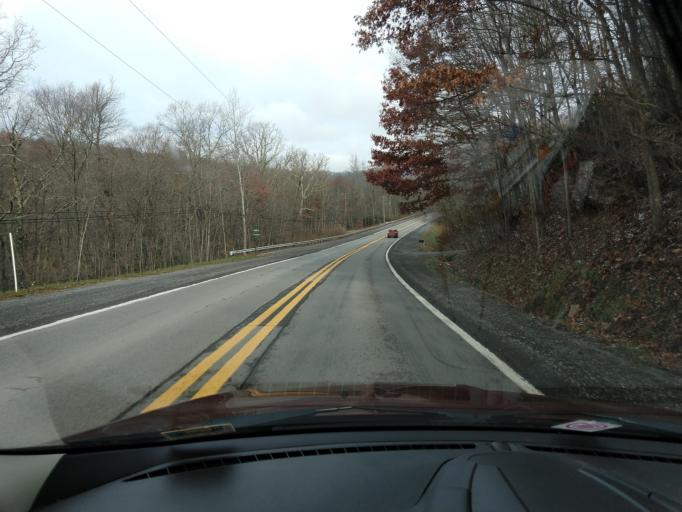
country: US
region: West Virginia
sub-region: Greenbrier County
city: Rainelle
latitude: 38.0349
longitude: -80.7295
